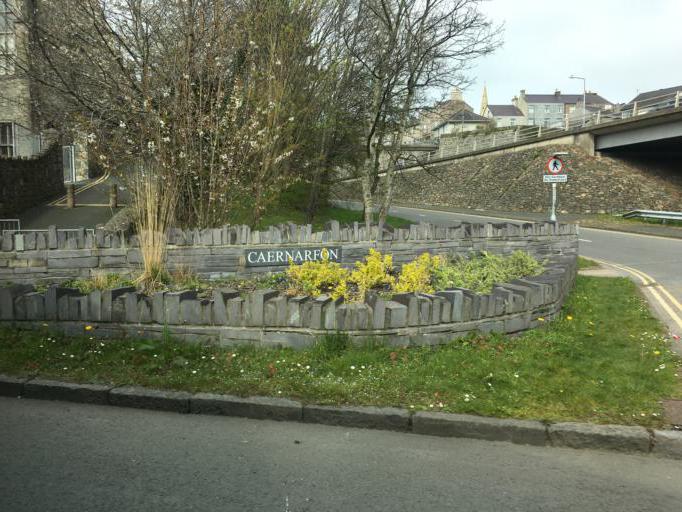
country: GB
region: Wales
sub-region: Gwynedd
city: Caernarfon
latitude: 53.1400
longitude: -4.2713
